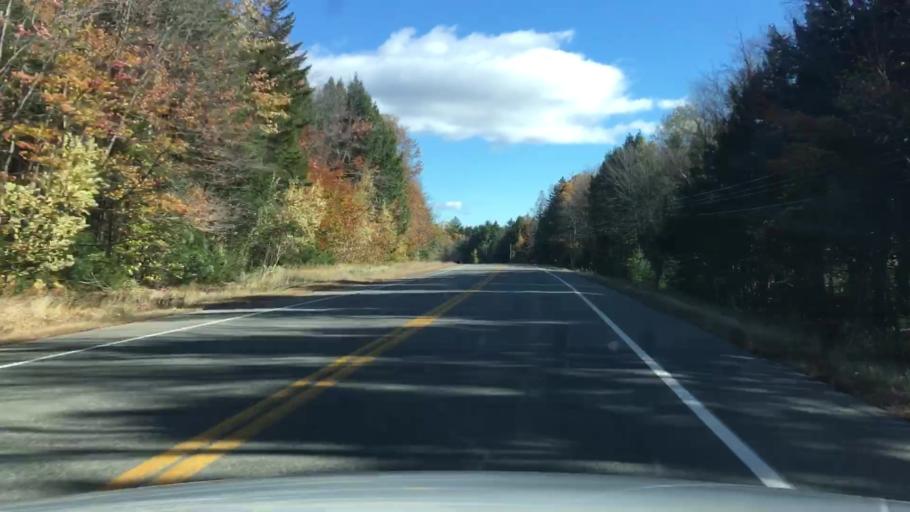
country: US
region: Maine
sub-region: Penobscot County
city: Millinocket
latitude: 45.6567
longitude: -68.6582
